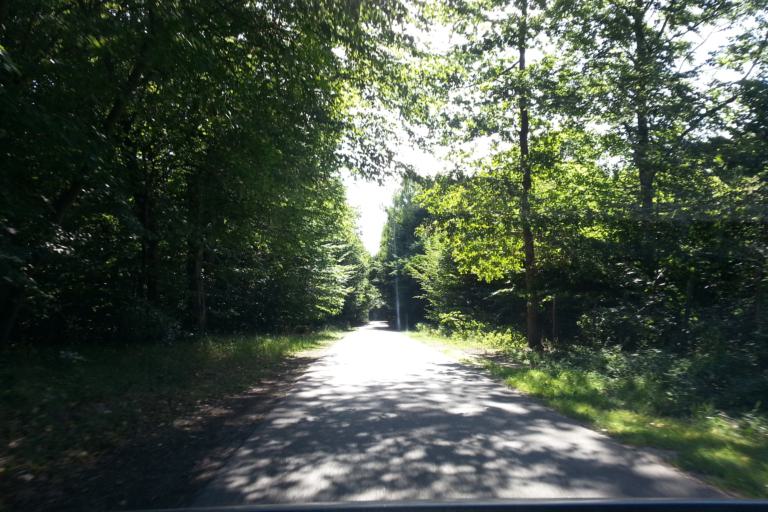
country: DE
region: Mecklenburg-Vorpommern
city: Torgelow
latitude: 53.6551
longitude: 14.0337
